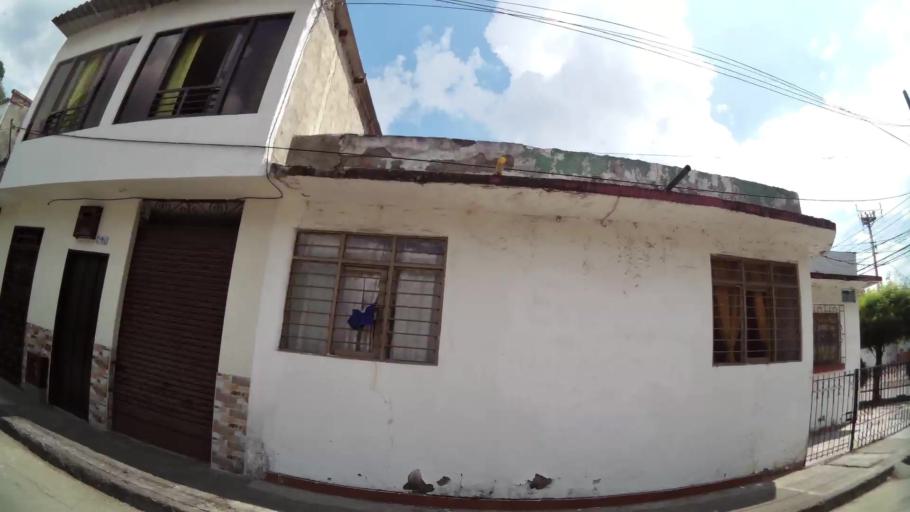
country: CO
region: Valle del Cauca
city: Cali
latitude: 3.4650
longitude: -76.5051
